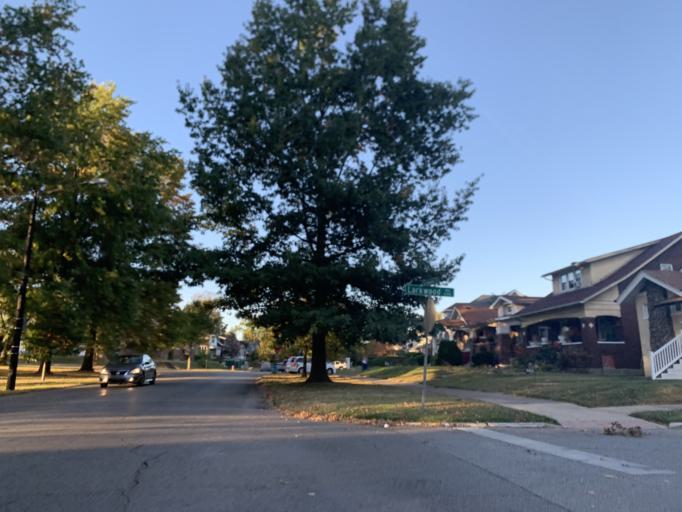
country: US
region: Indiana
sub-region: Floyd County
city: New Albany
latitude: 38.2595
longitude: -85.8239
